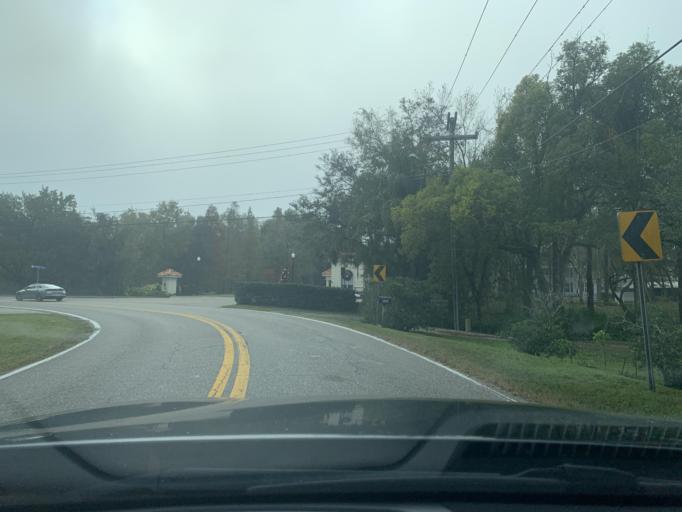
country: US
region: Florida
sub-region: Hillsborough County
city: Lutz
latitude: 28.1180
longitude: -82.4742
